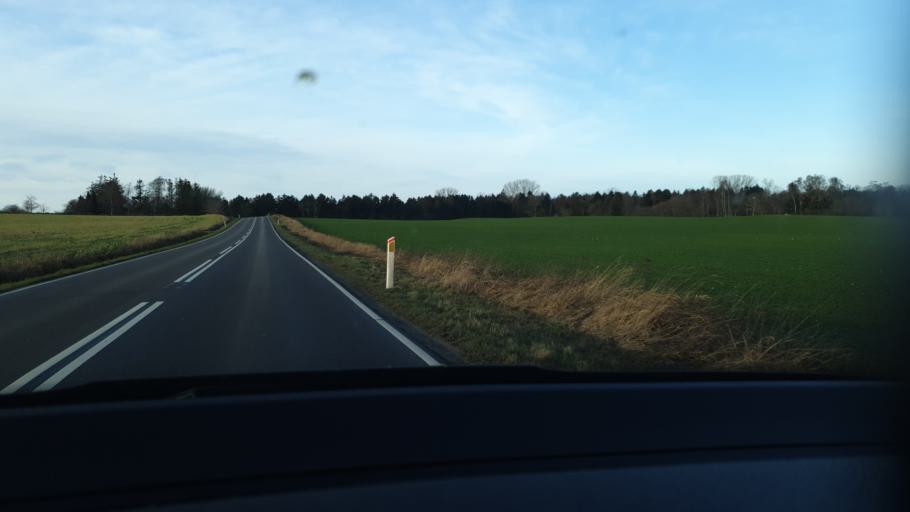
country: DK
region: Zealand
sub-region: Odsherred Kommune
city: Hojby
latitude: 55.9275
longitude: 11.6308
